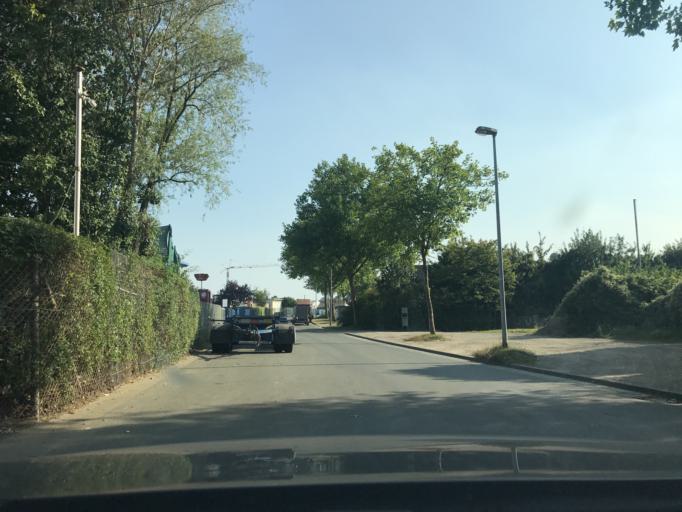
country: DE
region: North Rhine-Westphalia
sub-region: Regierungsbezirk Dusseldorf
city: Kleve
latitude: 51.8055
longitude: 6.1370
